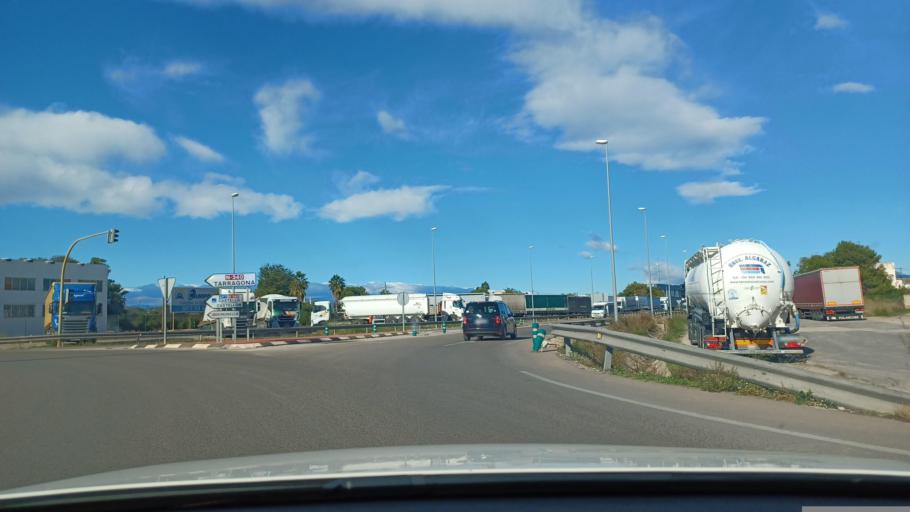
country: ES
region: Valencia
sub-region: Provincia de Castello
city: Vinaros
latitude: 40.4710
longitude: 0.4655
